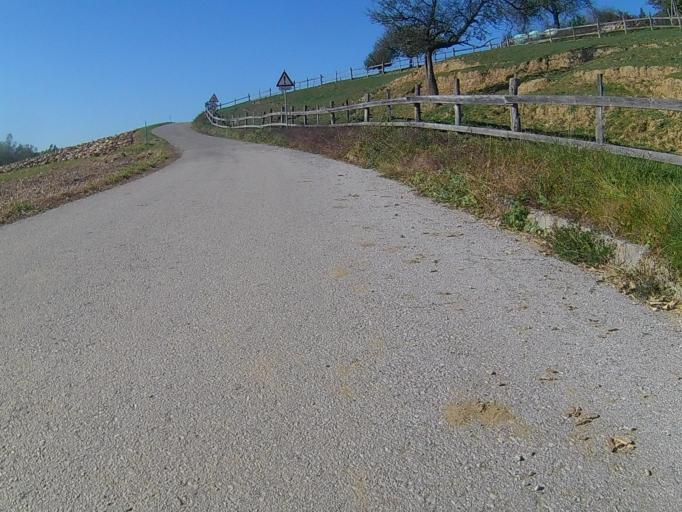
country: SI
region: Sveti Jurij v Slovenskih Goricah
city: Jurovski Dol
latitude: 46.5761
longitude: 15.7487
